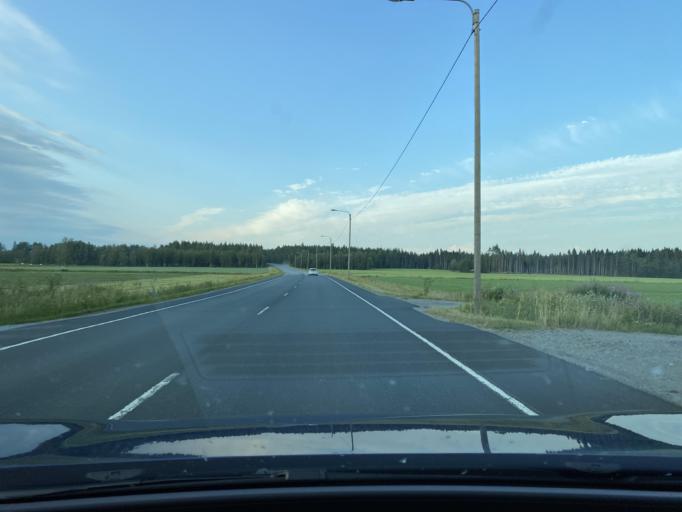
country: FI
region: Ostrobothnia
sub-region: Jakobstadsregionen
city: Bennaes
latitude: 63.6388
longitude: 22.8767
